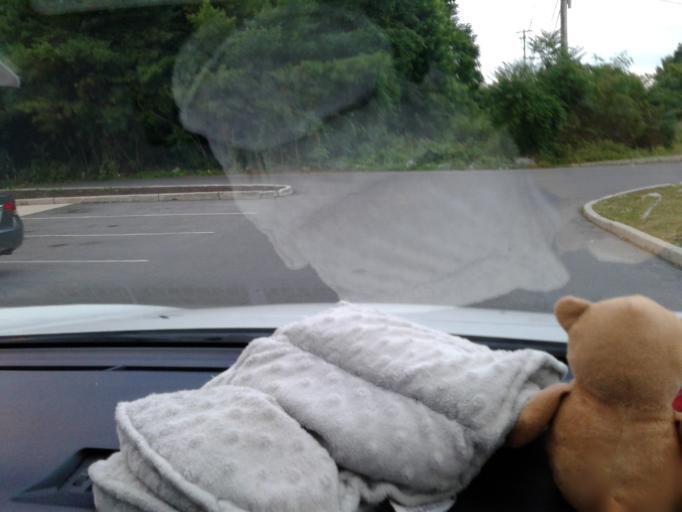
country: US
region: West Virginia
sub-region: Berkeley County
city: Martinsburg
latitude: 39.4780
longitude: -77.9592
